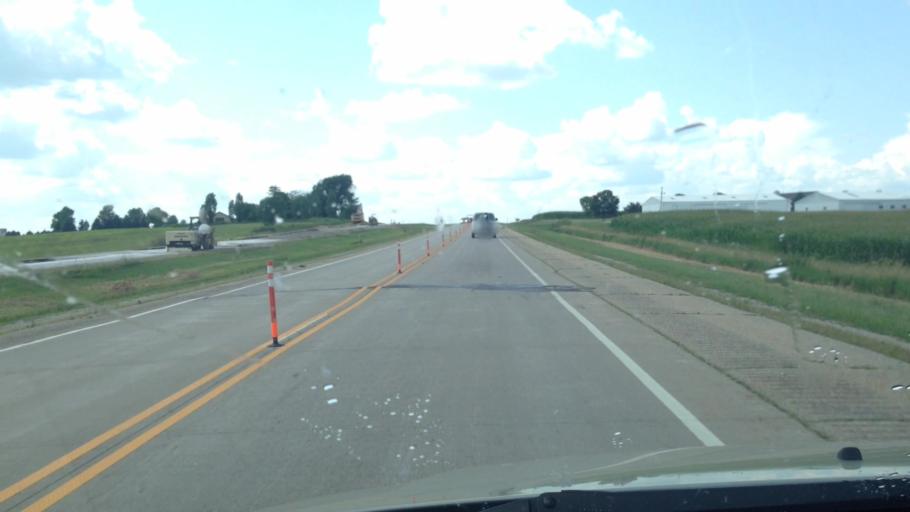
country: US
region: Wisconsin
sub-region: Shawano County
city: Bonduel
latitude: 44.6971
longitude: -88.3509
